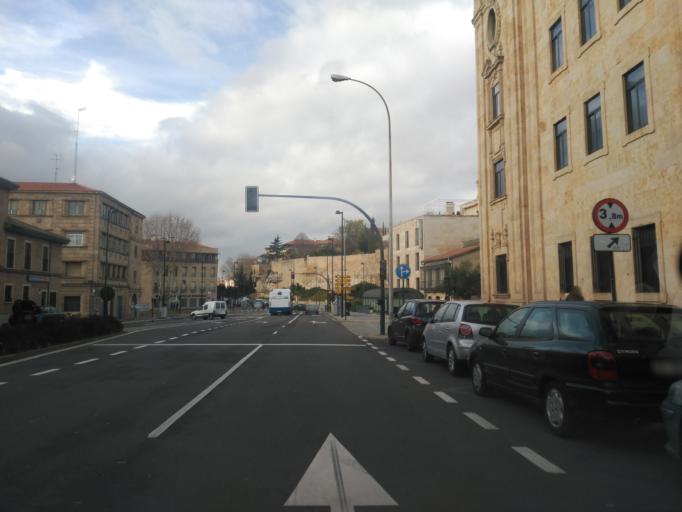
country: ES
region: Castille and Leon
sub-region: Provincia de Salamanca
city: Salamanca
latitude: 40.9587
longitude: -5.6635
